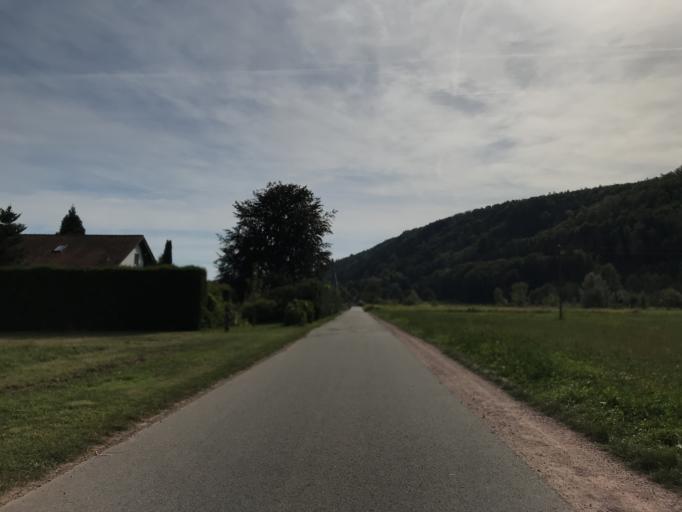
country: DE
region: Baden-Wuerttemberg
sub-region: Freiburg Region
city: Hausen
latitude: 47.6699
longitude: 7.8331
